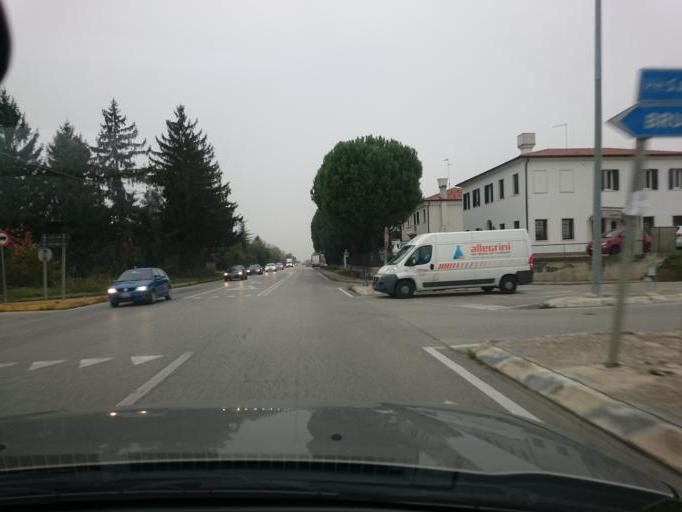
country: IT
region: Veneto
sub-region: Provincia di Padova
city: Legnaro
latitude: 45.3300
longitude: 11.9869
